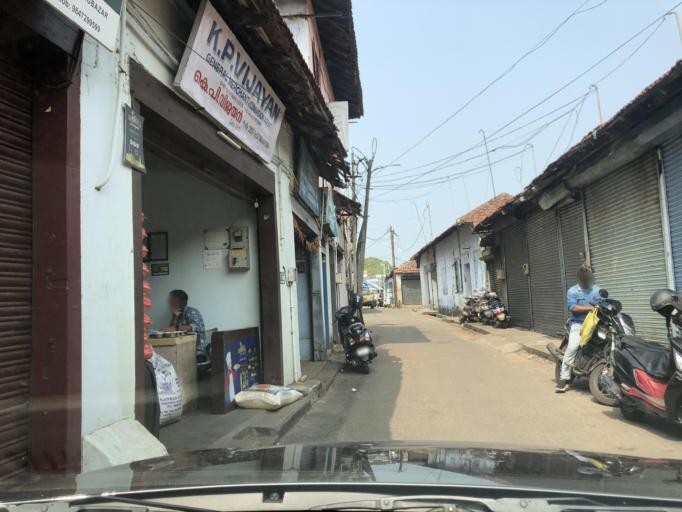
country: IN
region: Kerala
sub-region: Kozhikode
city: Kozhikode
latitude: 11.2492
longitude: 75.7754
